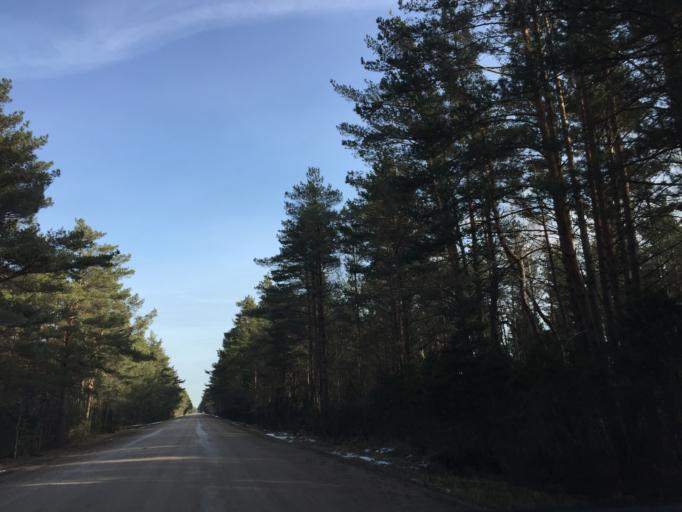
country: EE
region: Saare
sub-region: Kuressaare linn
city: Kuressaare
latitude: 58.2968
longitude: 21.9499
